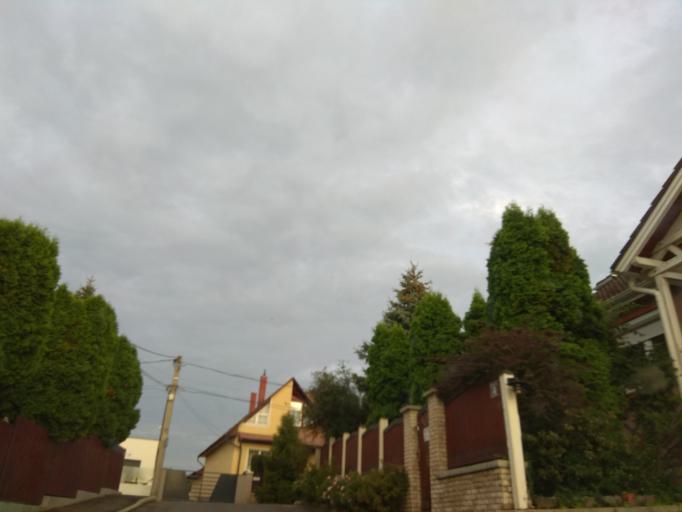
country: HU
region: Borsod-Abauj-Zemplen
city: Miskolc
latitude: 48.0544
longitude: 20.7883
